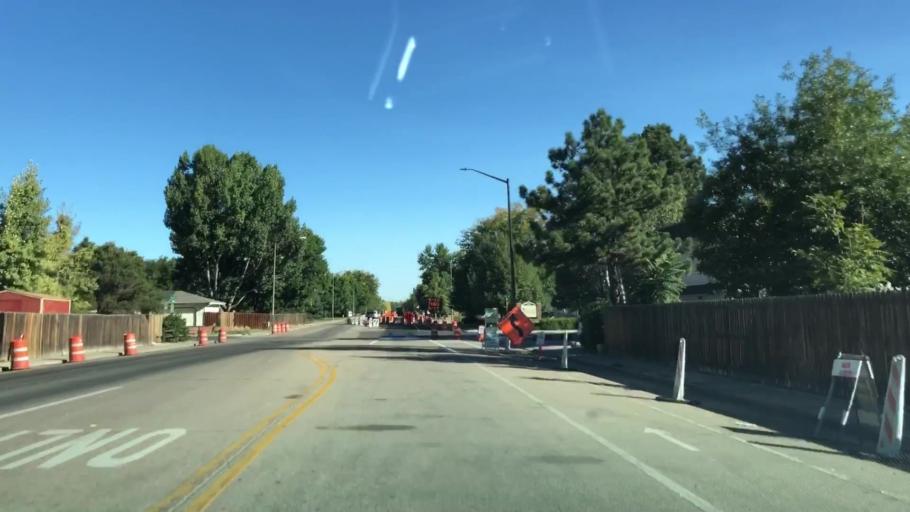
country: US
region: Colorado
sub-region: Larimer County
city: Loveland
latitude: 40.4096
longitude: -105.0537
